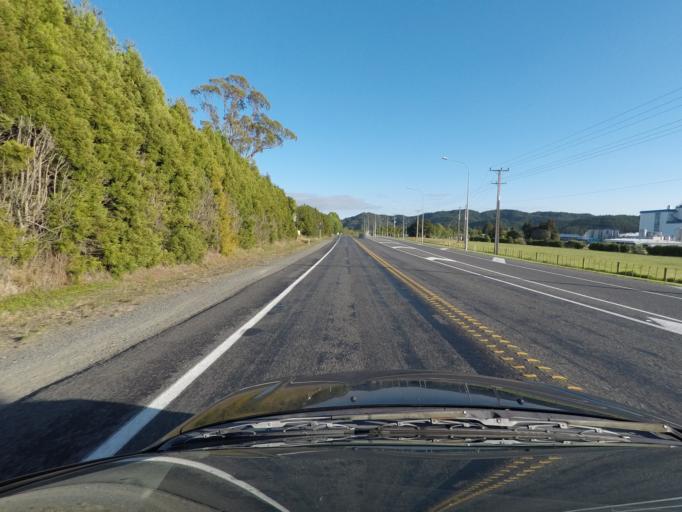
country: NZ
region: Northland
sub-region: Whangarei
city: Whangarei
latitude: -35.6373
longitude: 174.2966
